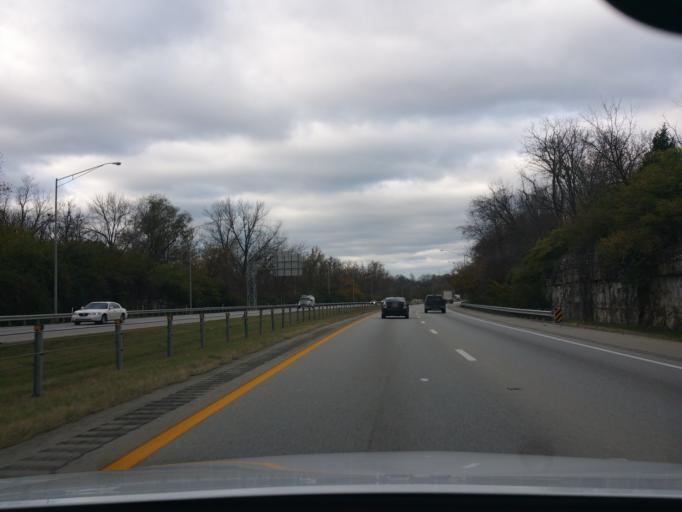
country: US
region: Kentucky
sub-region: Jefferson County
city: Saint Matthews
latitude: 38.2358
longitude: -85.6503
